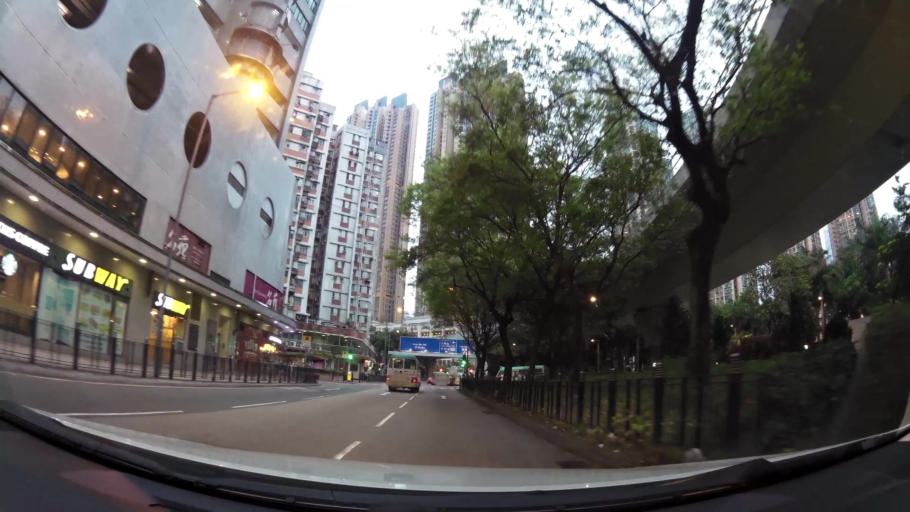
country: HK
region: Sham Shui Po
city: Sham Shui Po
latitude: 22.3194
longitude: 114.1623
